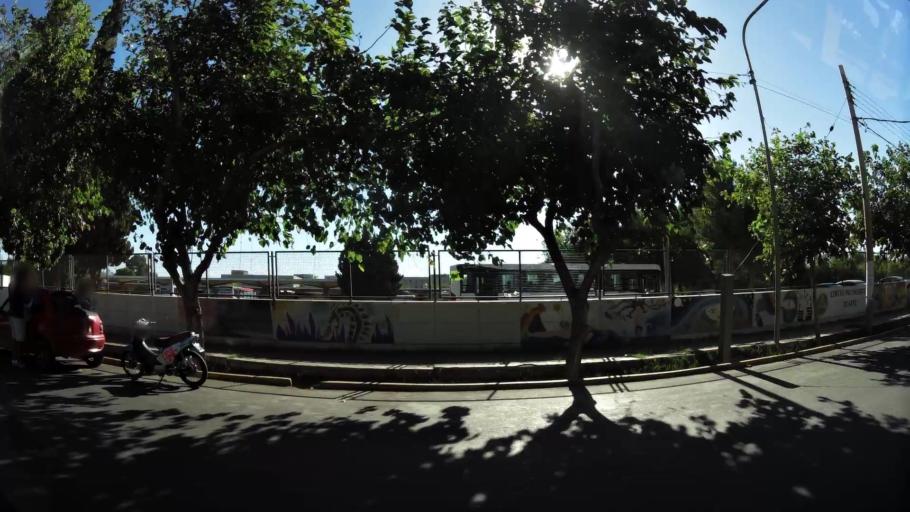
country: AR
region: San Juan
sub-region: Departamento de Santa Lucia
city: Santa Lucia
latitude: -31.5389
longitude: -68.5099
